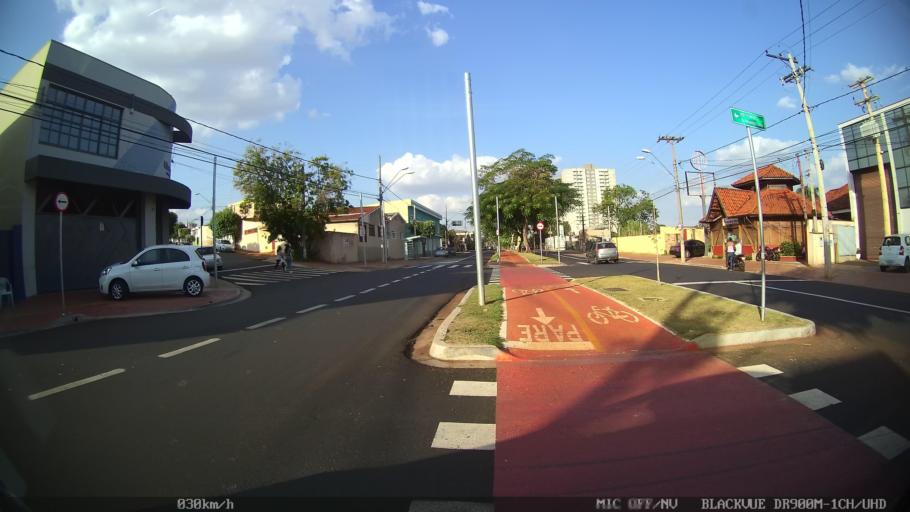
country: BR
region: Sao Paulo
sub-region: Ribeirao Preto
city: Ribeirao Preto
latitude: -21.1749
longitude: -47.8330
